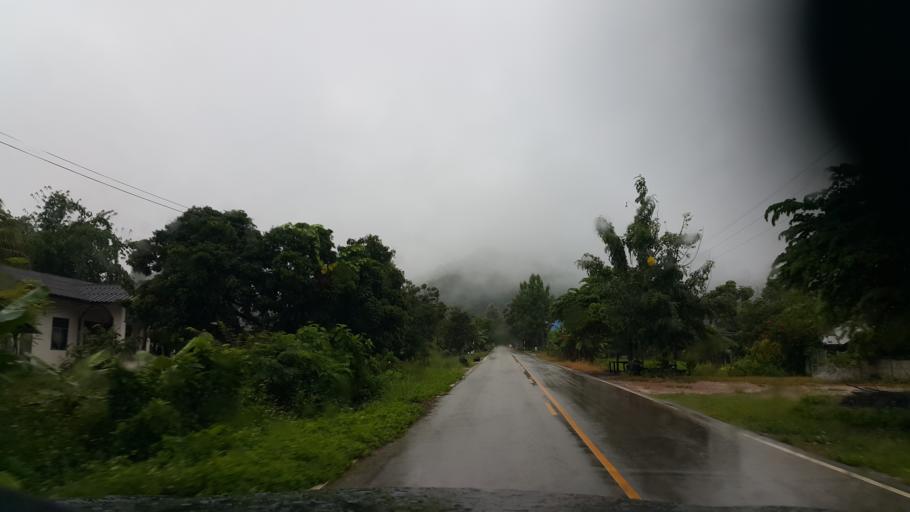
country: TH
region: Phayao
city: Phu Sang
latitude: 19.6036
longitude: 100.4027
